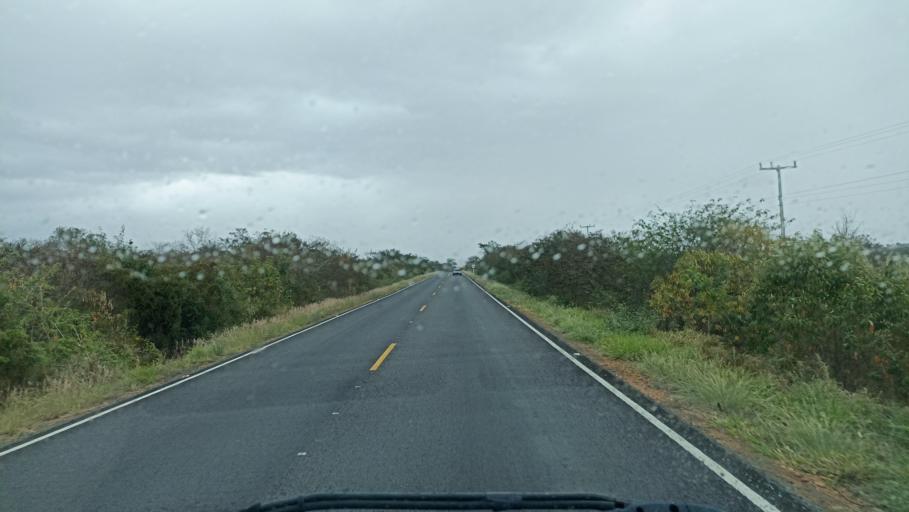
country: BR
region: Bahia
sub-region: Maracas
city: Maracas
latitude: -13.0420
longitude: -40.7043
